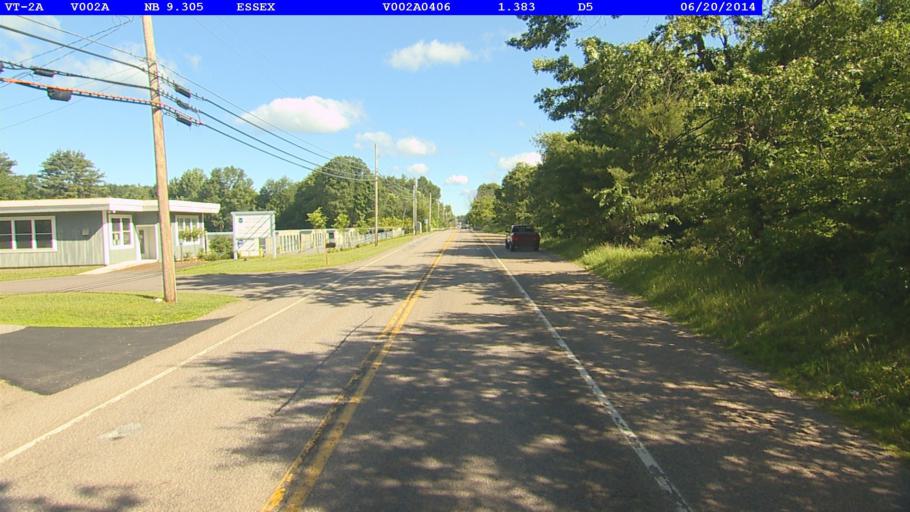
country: US
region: Vermont
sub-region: Chittenden County
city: Essex Junction
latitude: 44.5006
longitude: -73.1140
